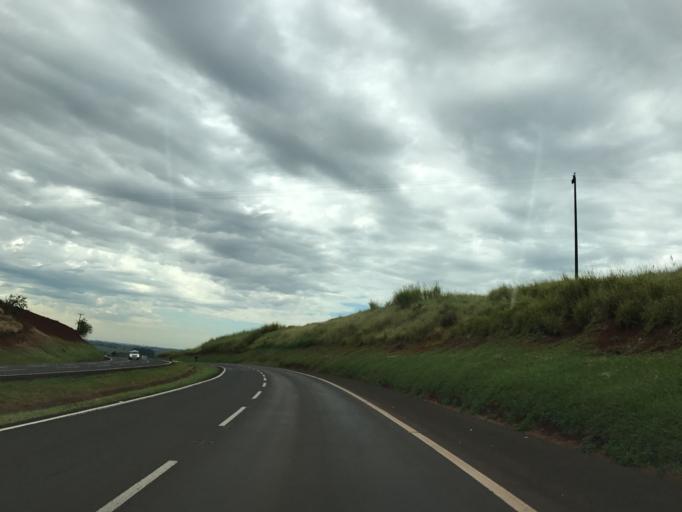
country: BR
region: Parana
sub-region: Rolandia
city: Rolandia
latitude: -23.3406
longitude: -51.3556
